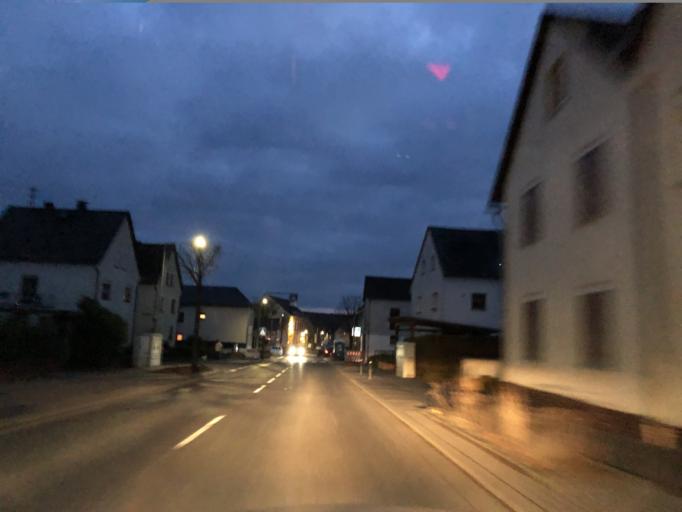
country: DE
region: Rheinland-Pfalz
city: Singhofen
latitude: 50.2765
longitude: 7.8361
